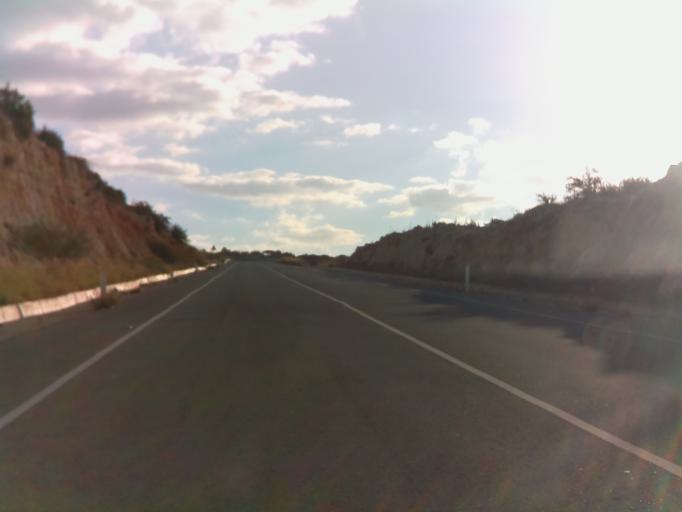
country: CY
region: Pafos
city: Pegeia
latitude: 34.8879
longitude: 32.3512
